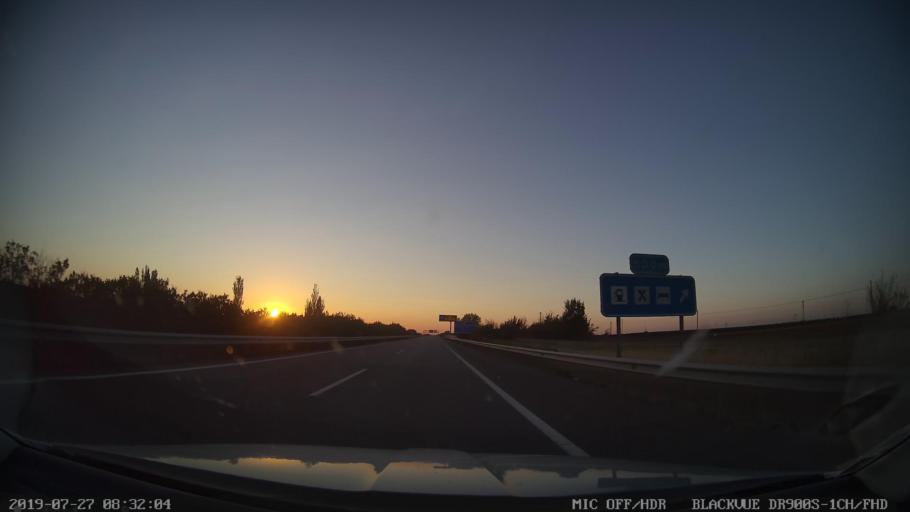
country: ES
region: Extremadura
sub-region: Provincia de Badajoz
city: Talavera La Real
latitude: 38.8593
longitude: -6.7470
